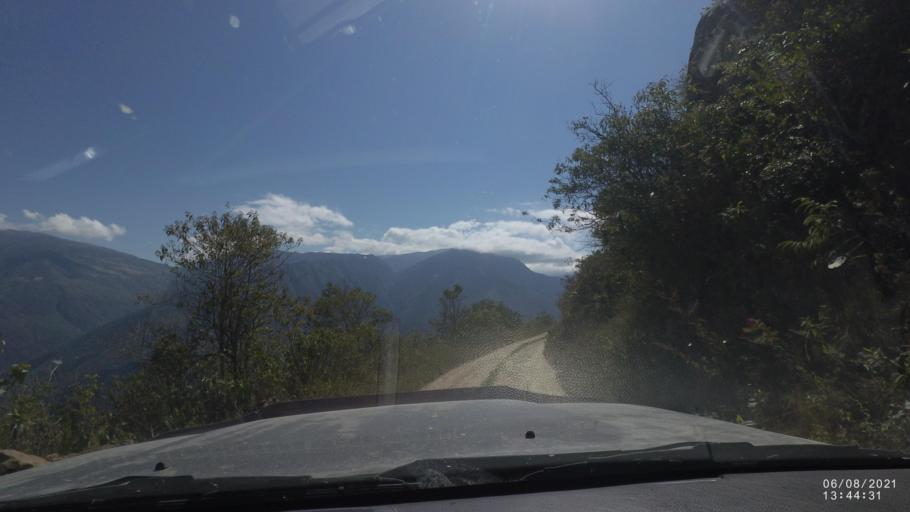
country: BO
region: La Paz
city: Quime
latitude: -16.6752
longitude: -66.7327
